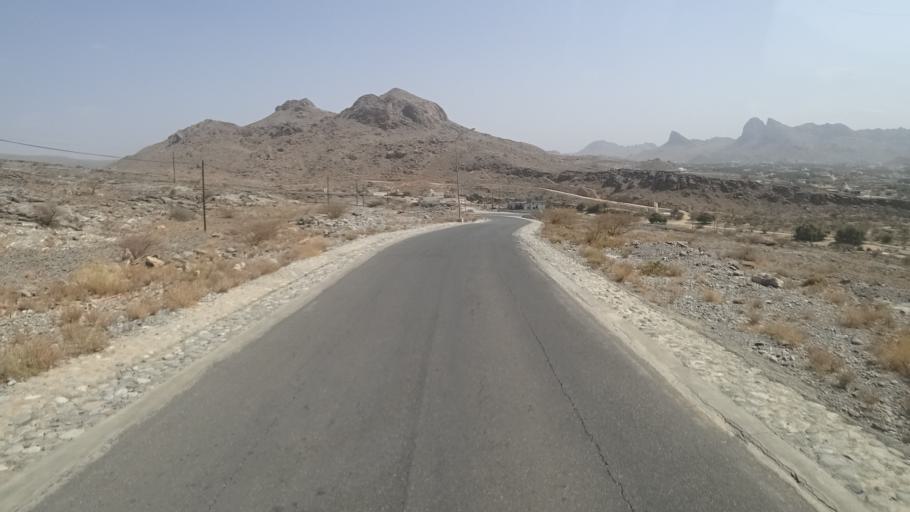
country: OM
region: Muhafazat ad Dakhiliyah
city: Bahla'
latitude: 23.1265
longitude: 57.2973
